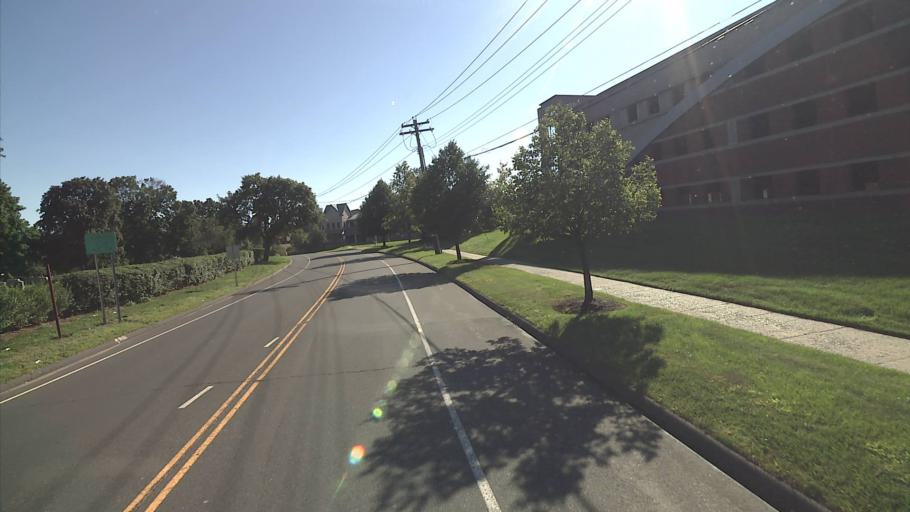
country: US
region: Connecticut
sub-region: New Haven County
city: New Haven
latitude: 41.3361
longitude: -72.9434
